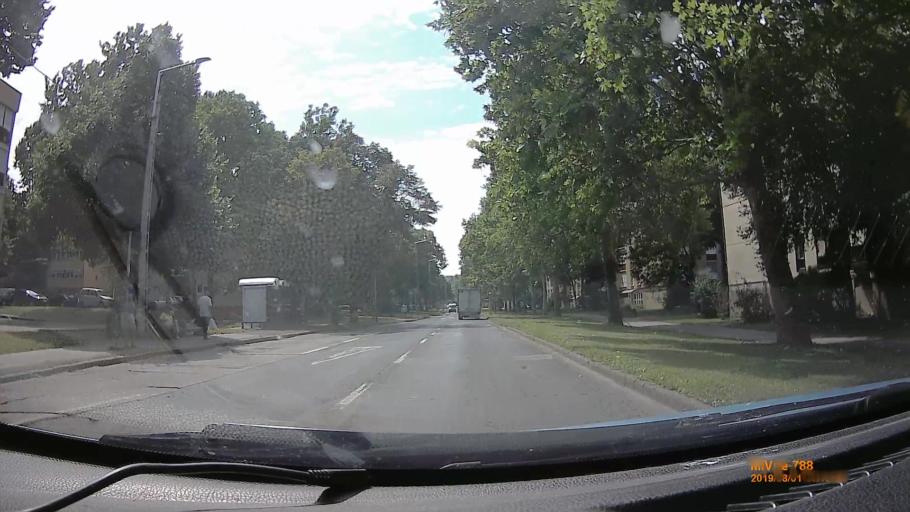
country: HU
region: Baranya
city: Pecs
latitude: 46.0464
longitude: 18.2146
